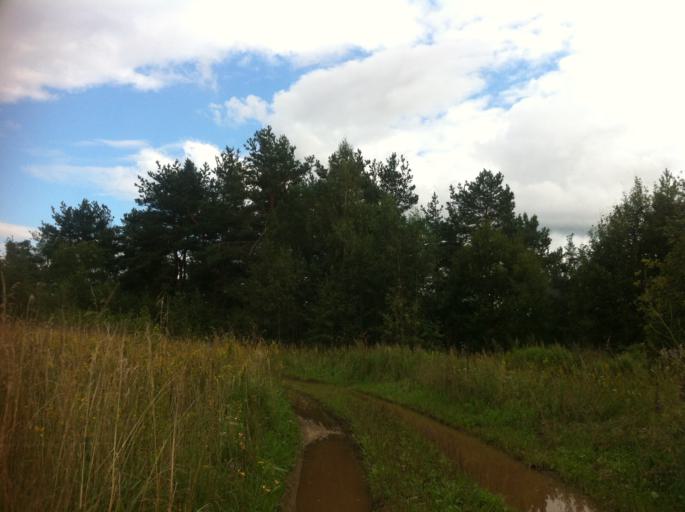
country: RU
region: Pskov
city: Izborsk
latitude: 57.8202
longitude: 27.9691
